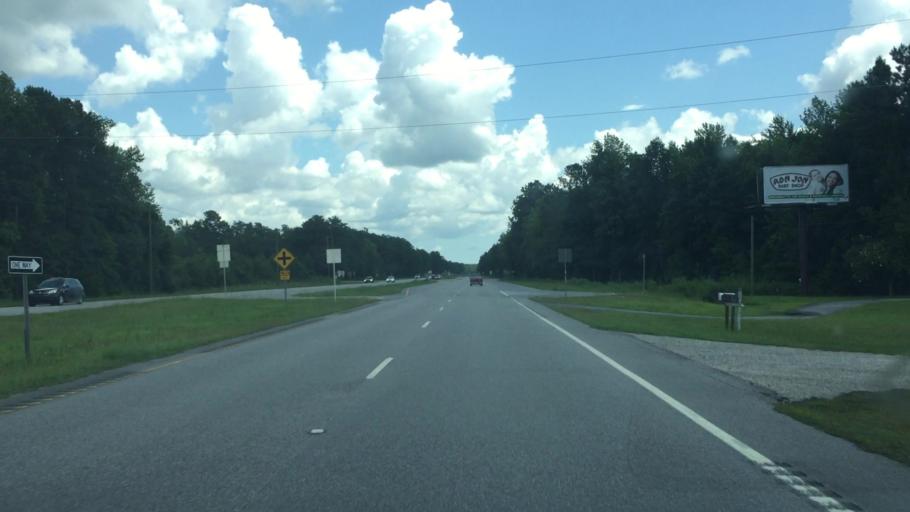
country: US
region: South Carolina
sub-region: Horry County
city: Loris
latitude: 34.0412
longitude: -78.8222
